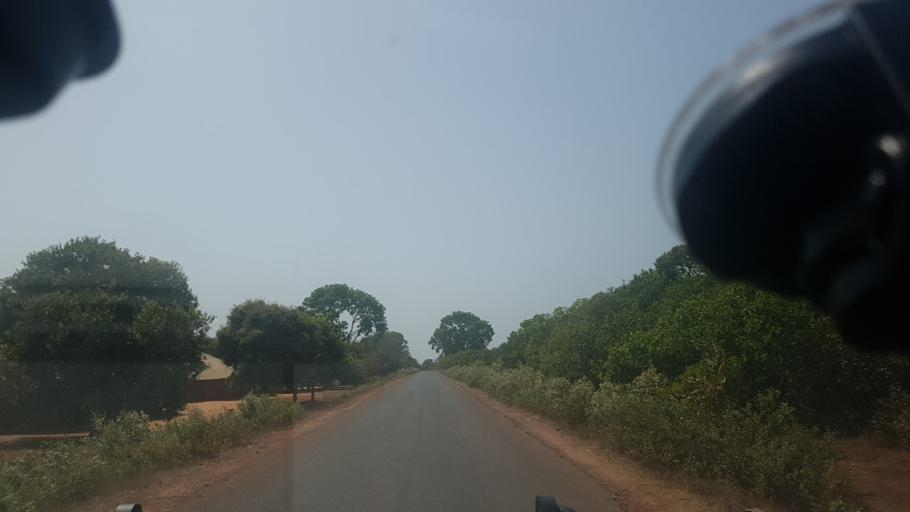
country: GW
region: Cacheu
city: Cacheu
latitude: 12.4115
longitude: -16.0672
